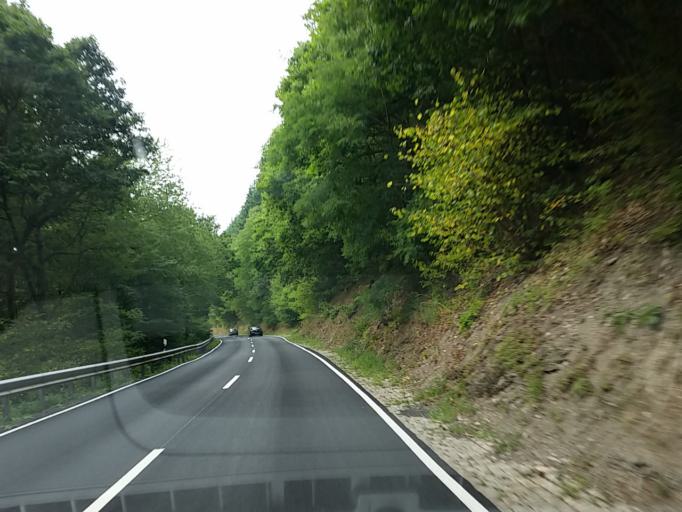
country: DE
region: Rheinland-Pfalz
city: Osburg
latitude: 49.7353
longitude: 6.7754
